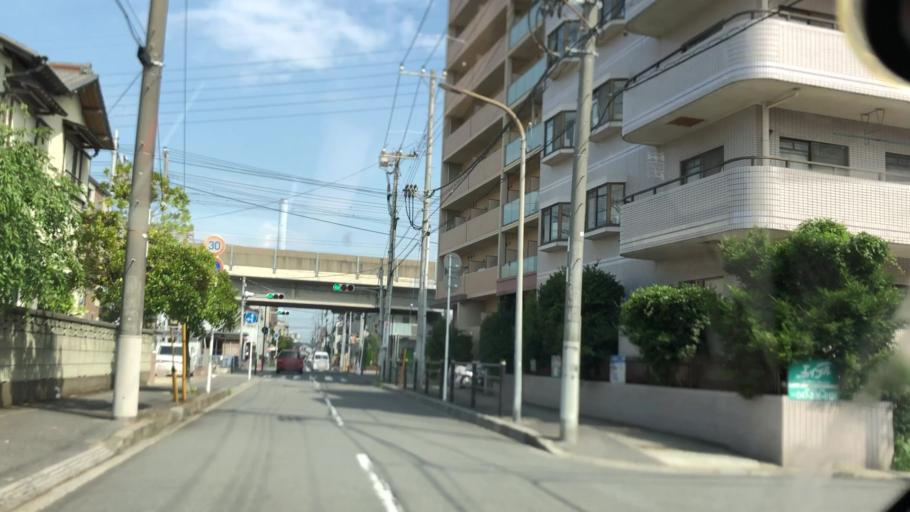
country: JP
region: Tokyo
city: Urayasu
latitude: 35.6788
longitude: 139.9107
